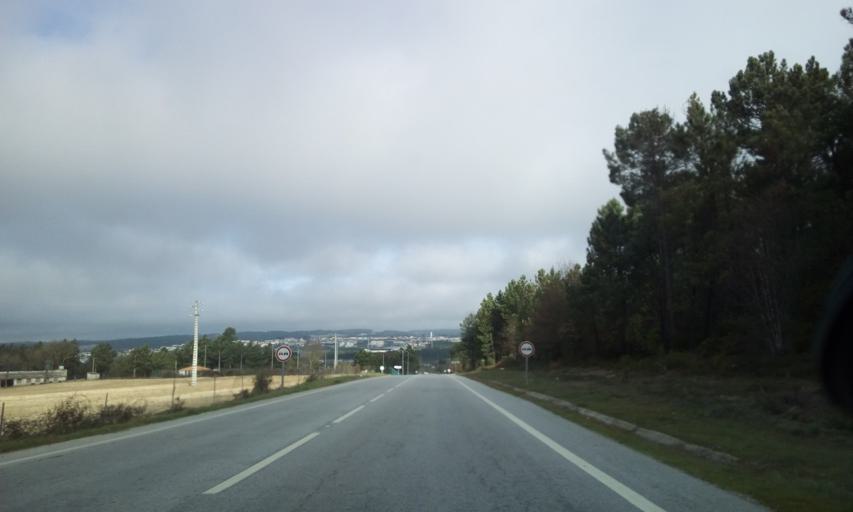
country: PT
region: Guarda
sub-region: Aguiar da Beira
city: Aguiar da Beira
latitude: 40.8020
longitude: -7.5225
